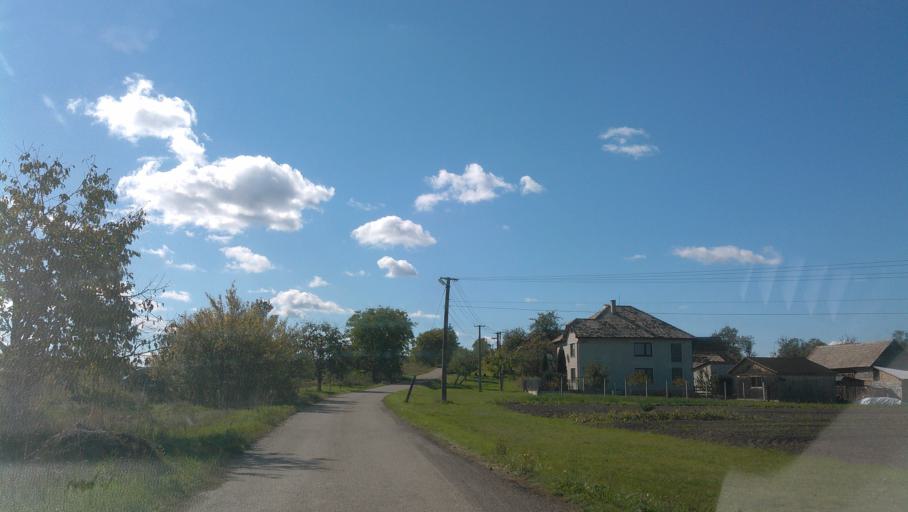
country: SK
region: Banskobystricky
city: Rimavska Sobota
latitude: 48.3462
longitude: 20.0401
